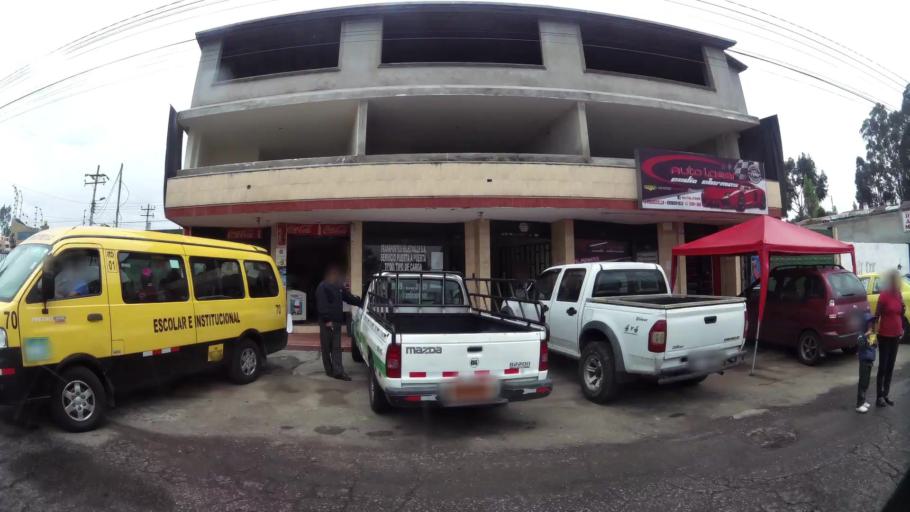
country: EC
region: Pichincha
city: Sangolqui
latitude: -0.3333
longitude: -78.4358
